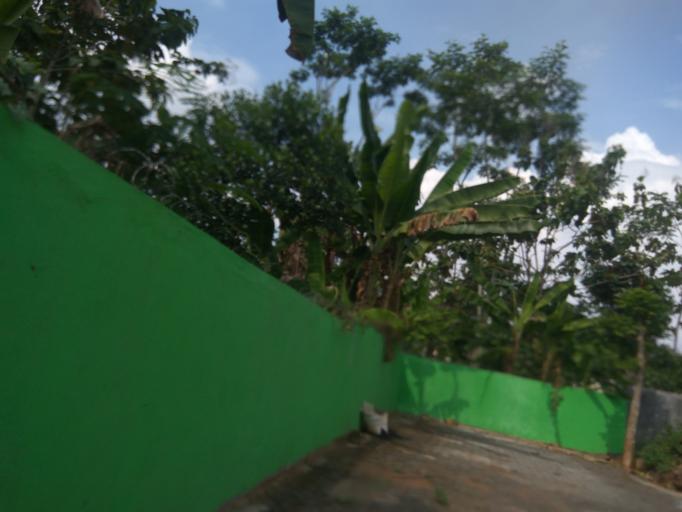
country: ID
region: Central Java
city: Ungaran
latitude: -7.0705
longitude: 110.4467
